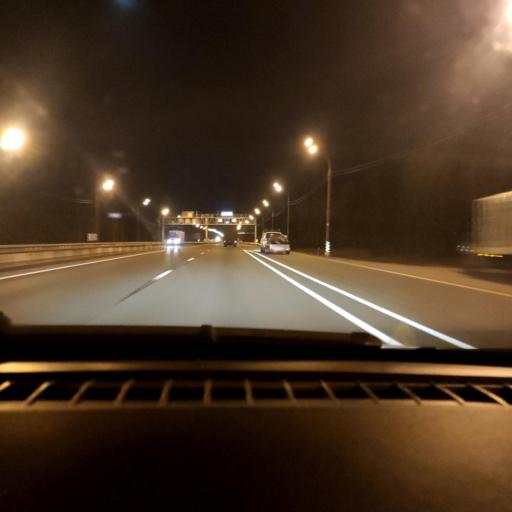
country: RU
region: Lipetsk
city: Khlevnoye
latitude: 52.2106
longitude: 39.1527
